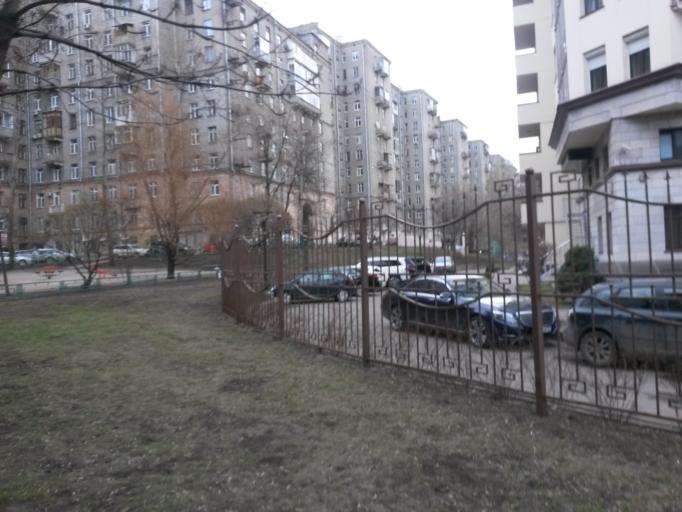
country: RU
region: Moscow
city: Vorob'yovo
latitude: 55.7385
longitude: 37.5213
